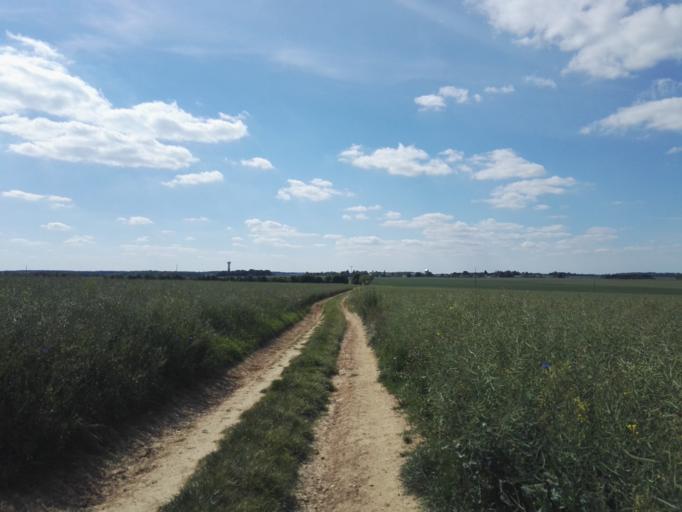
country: FR
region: Haute-Normandie
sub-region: Departement de l'Eure
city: Menilles
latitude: 49.0022
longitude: 1.3280
